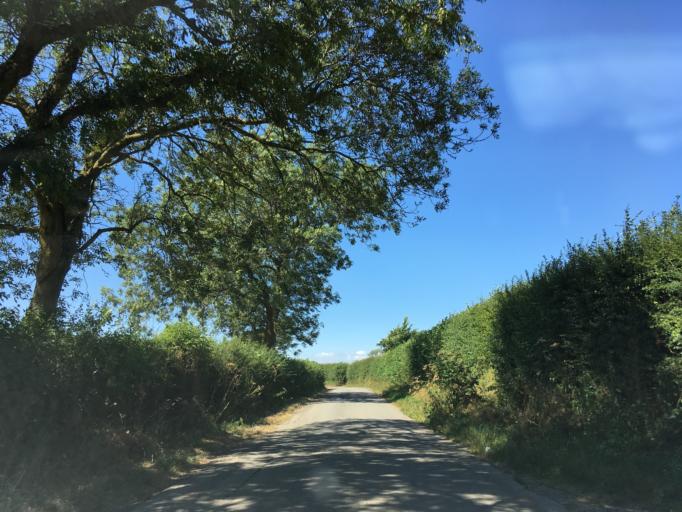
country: GB
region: England
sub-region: South Gloucestershire
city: Hinton
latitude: 51.5117
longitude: -2.3925
